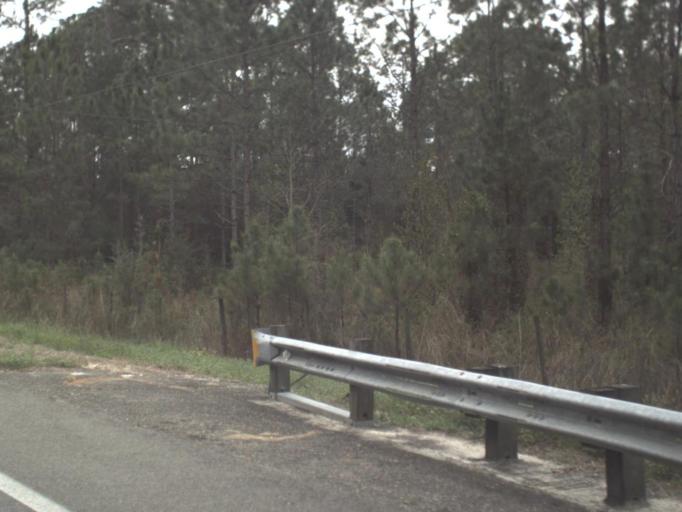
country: US
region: Florida
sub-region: Gulf County
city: Wewahitchka
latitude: 30.0709
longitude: -85.1935
